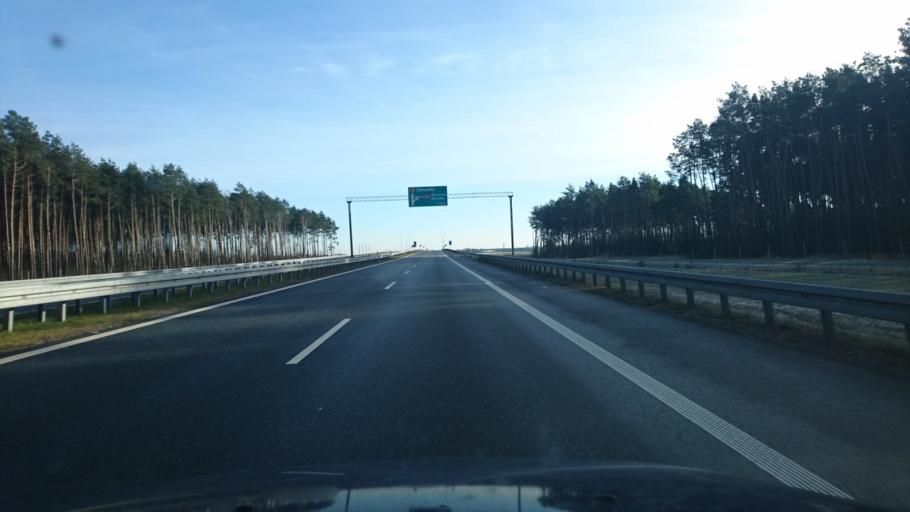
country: PL
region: Greater Poland Voivodeship
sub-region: Powiat kepinski
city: Kepno
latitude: 51.3253
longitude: 17.9920
